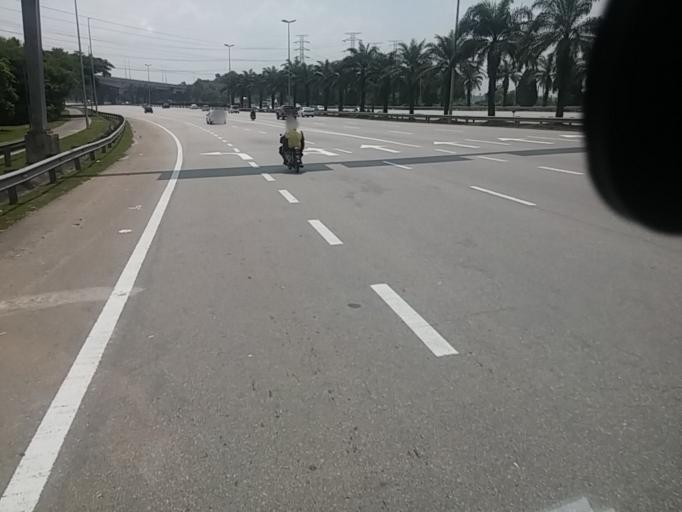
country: MY
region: Putrajaya
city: Putrajaya
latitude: 2.9678
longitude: 101.6647
